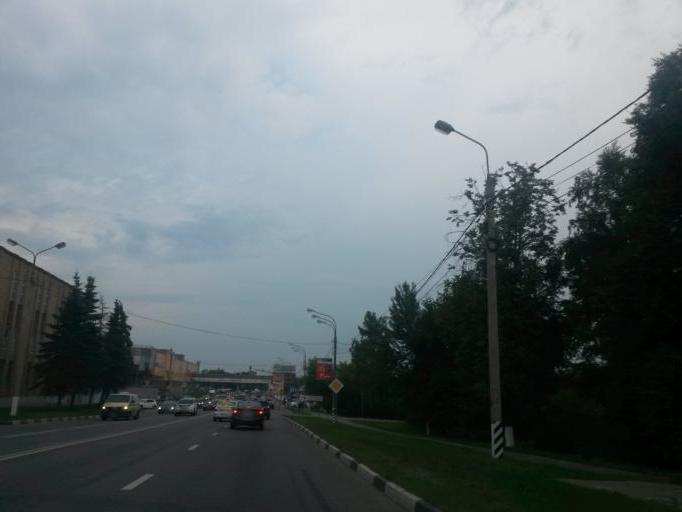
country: RU
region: Moskovskaya
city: Domodedovo
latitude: 55.4541
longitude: 37.7609
